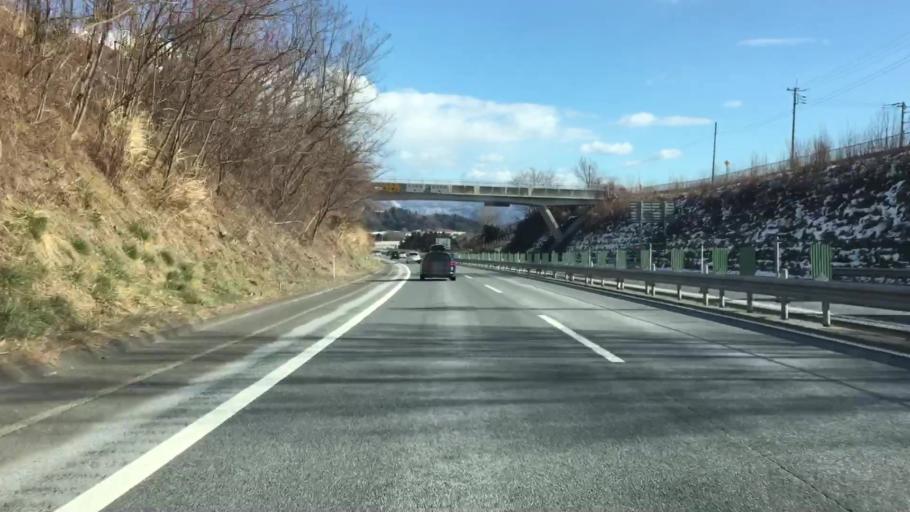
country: JP
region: Gunma
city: Numata
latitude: 36.6731
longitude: 139.0338
